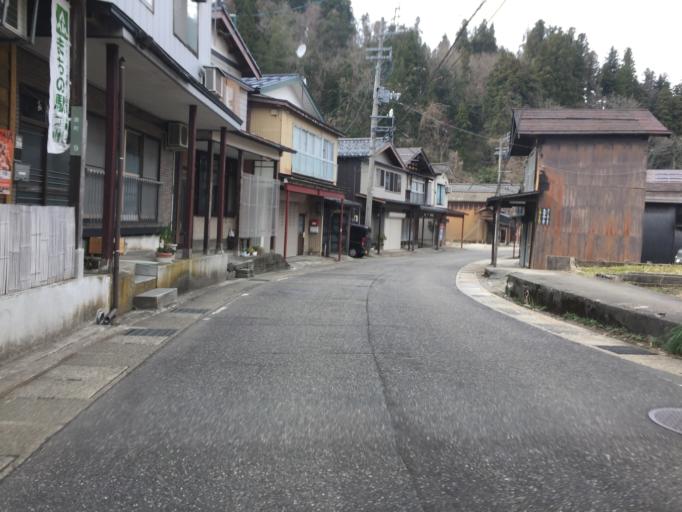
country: JP
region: Niigata
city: Tochio-honcho
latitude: 37.4723
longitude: 138.9922
